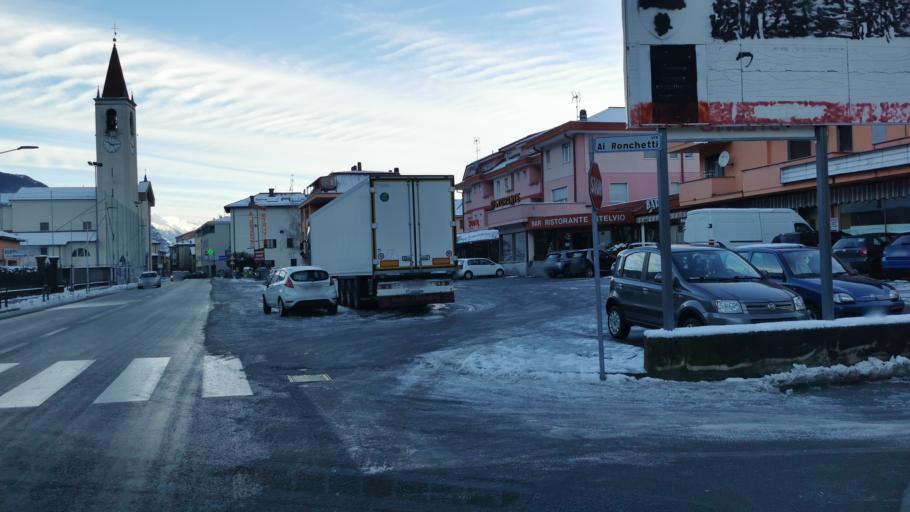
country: IT
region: Lombardy
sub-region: Provincia di Sondrio
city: Delebio
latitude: 46.1377
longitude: 9.4664
